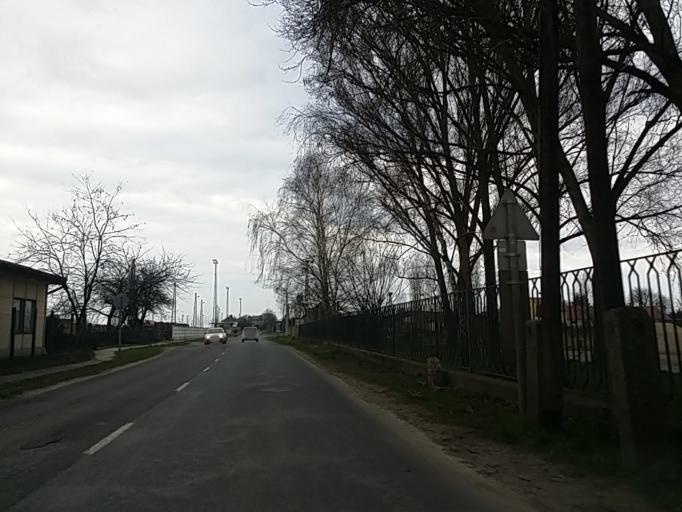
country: HU
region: Heves
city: Kal
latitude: 47.7355
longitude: 20.2602
